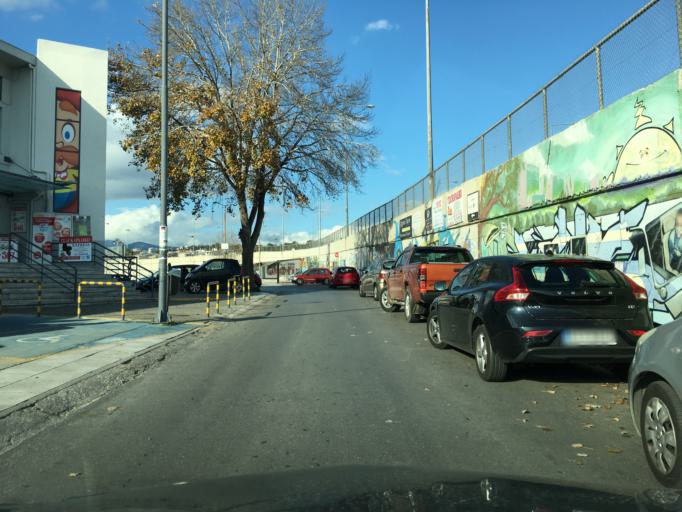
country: GR
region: Attica
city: Pefki
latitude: 38.0491
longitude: 23.7828
